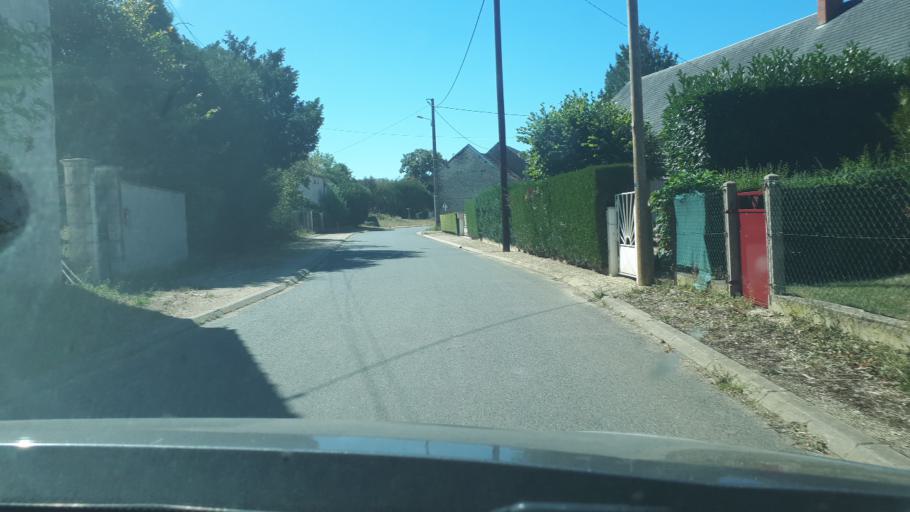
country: FR
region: Centre
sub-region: Departement du Cher
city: Baugy
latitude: 47.2042
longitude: 2.7367
